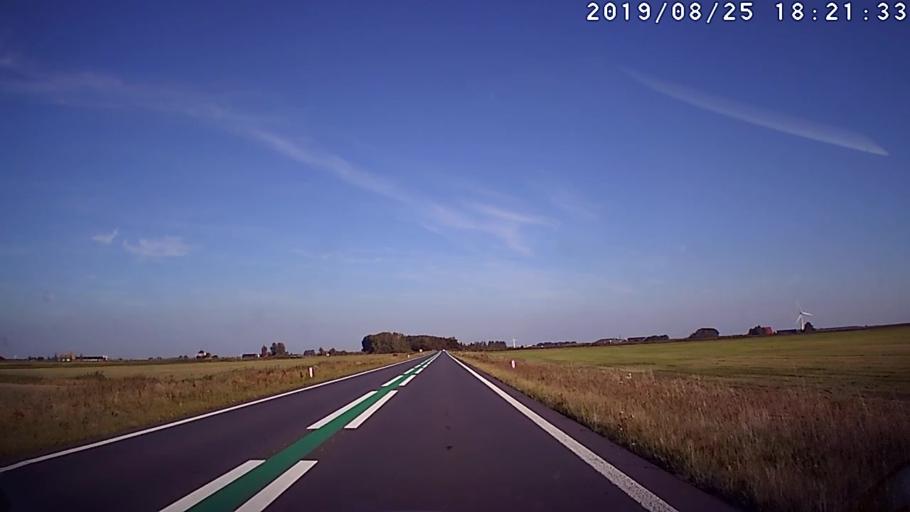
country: NL
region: Friesland
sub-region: Gemeente Gaasterlan-Sleat
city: Balk
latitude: 52.8713
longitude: 5.6333
